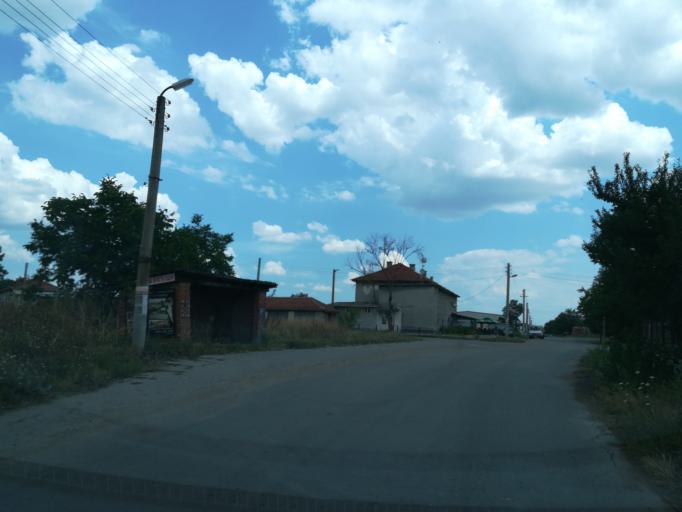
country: BG
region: Khaskovo
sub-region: Obshtina Mineralni Bani
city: Mineralni Bani
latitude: 41.9844
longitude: 25.1704
